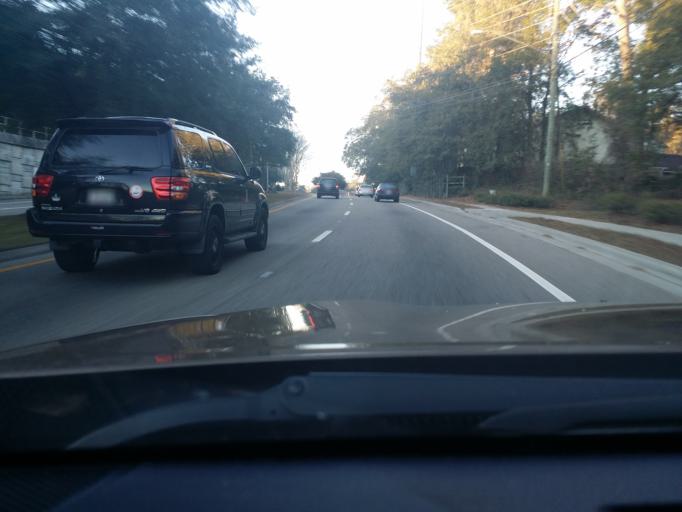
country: US
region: Florida
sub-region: Leon County
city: Tallahassee
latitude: 30.4619
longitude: -84.2453
